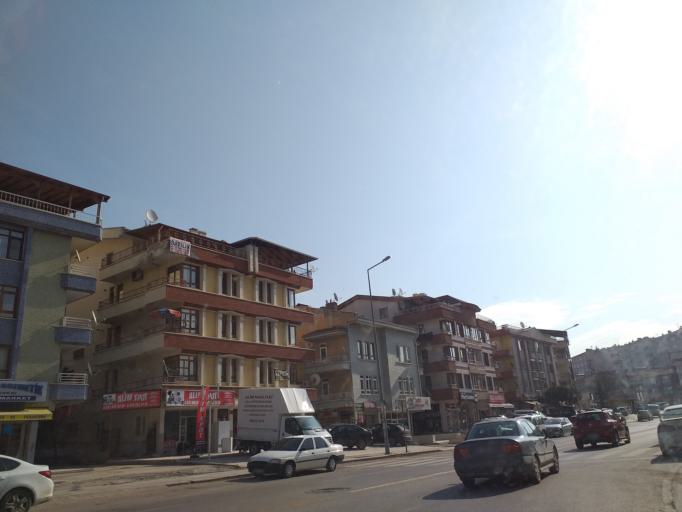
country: TR
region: Ankara
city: Ankara
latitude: 39.9854
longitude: 32.8495
